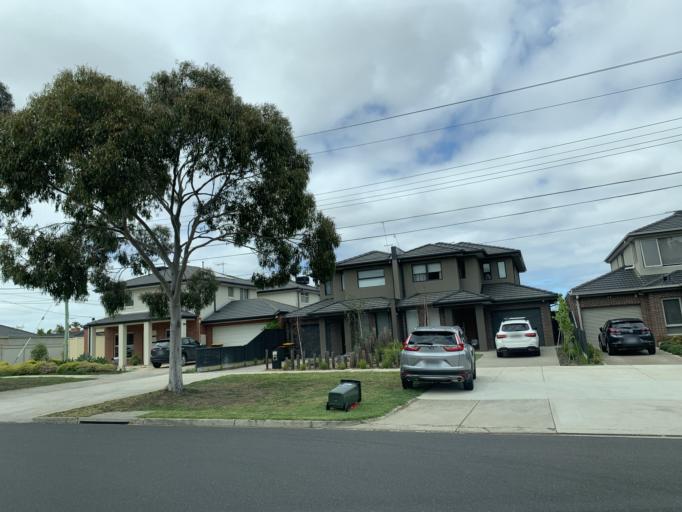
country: AU
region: Victoria
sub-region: Maribyrnong
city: Braybrook
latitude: -37.7697
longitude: 144.8572
